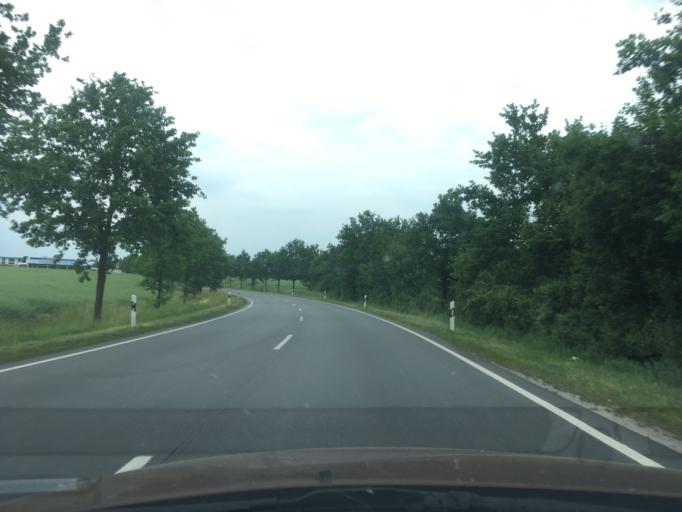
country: DE
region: Saxony
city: Bautzen
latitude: 51.1848
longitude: 14.4605
